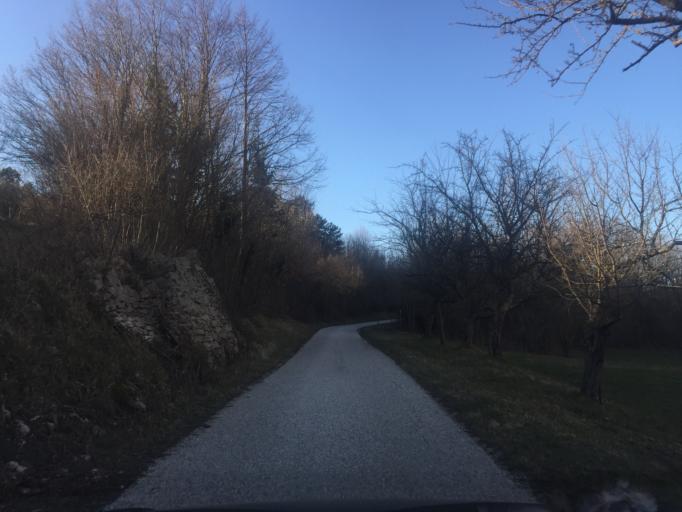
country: SI
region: Kanal
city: Deskle
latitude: 46.0344
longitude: 13.6654
